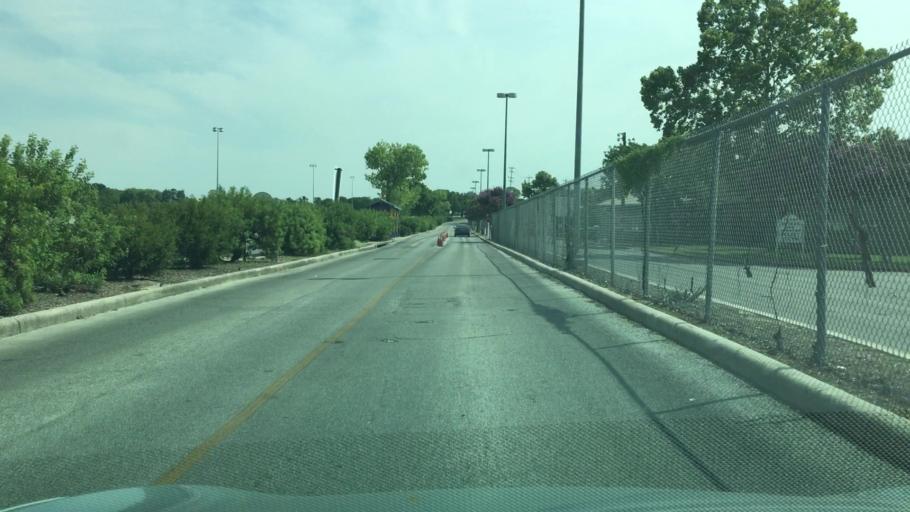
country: US
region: Texas
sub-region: Bexar County
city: Shavano Park
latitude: 29.6000
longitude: -98.6064
